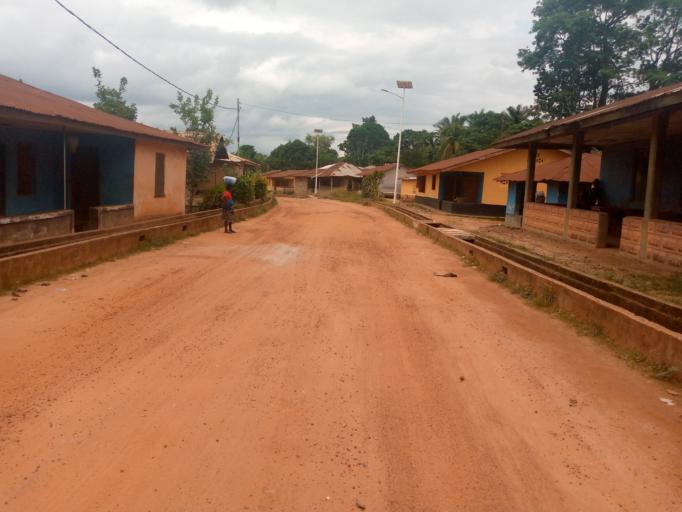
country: SL
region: Southern Province
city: Mogbwemo
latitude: 7.6097
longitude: -12.1801
